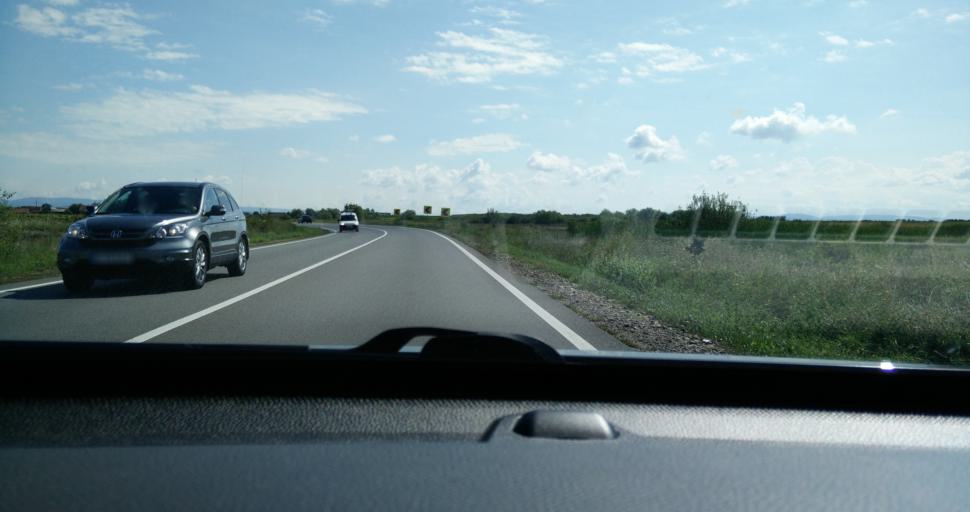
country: RO
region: Bihor
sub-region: Comuna Osorheiu
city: Osorheiu
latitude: 47.0521
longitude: 22.0661
